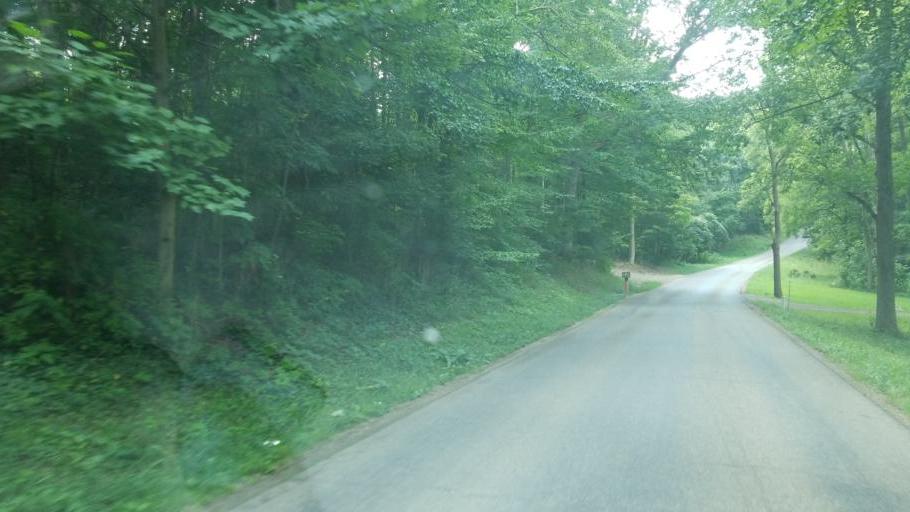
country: US
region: Ohio
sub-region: Knox County
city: Mount Vernon
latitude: 40.4252
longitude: -82.4701
